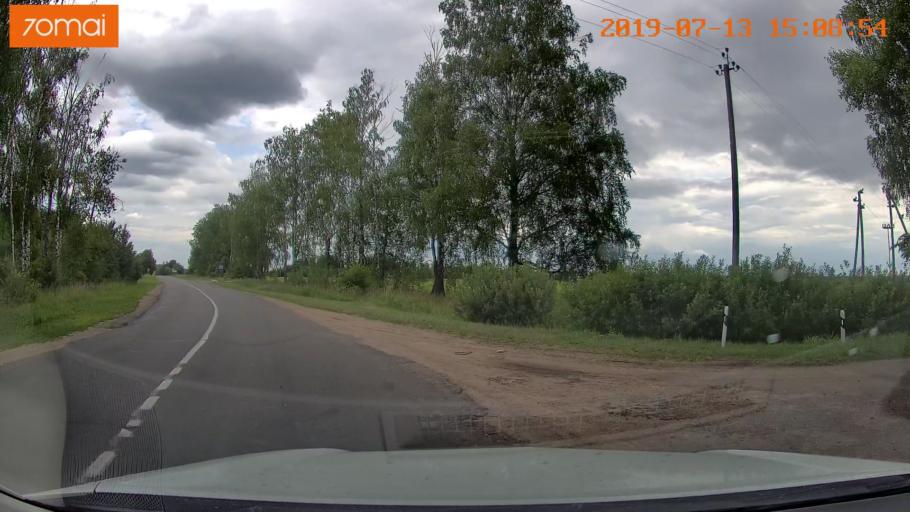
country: BY
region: Mogilev
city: Hlusha
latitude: 53.1748
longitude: 28.7545
